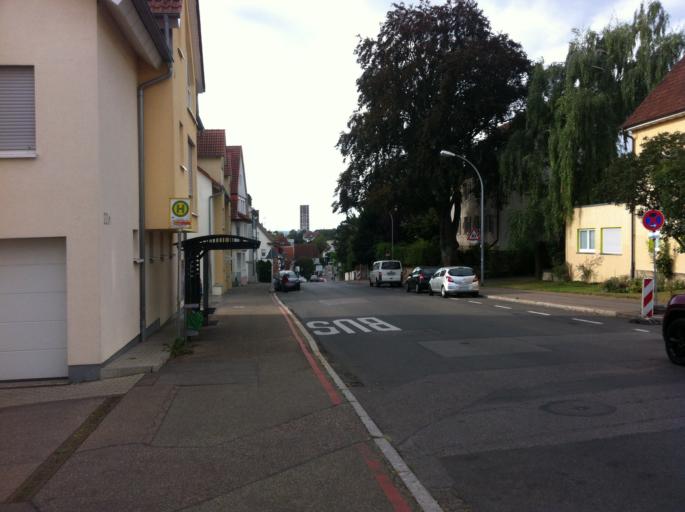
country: DE
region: Baden-Wuerttemberg
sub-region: Regierungsbezirk Stuttgart
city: Kornwestheim
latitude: 48.8674
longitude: 9.1862
